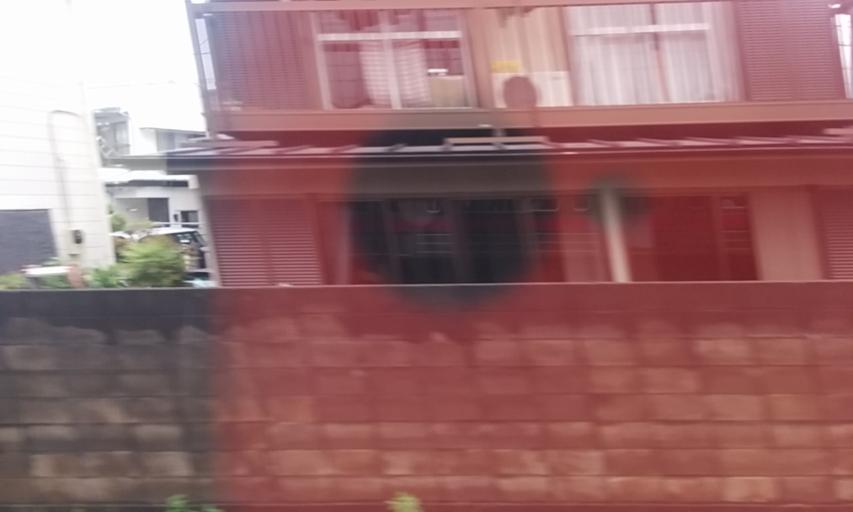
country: JP
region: Tokyo
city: Hino
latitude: 35.6591
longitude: 139.3969
